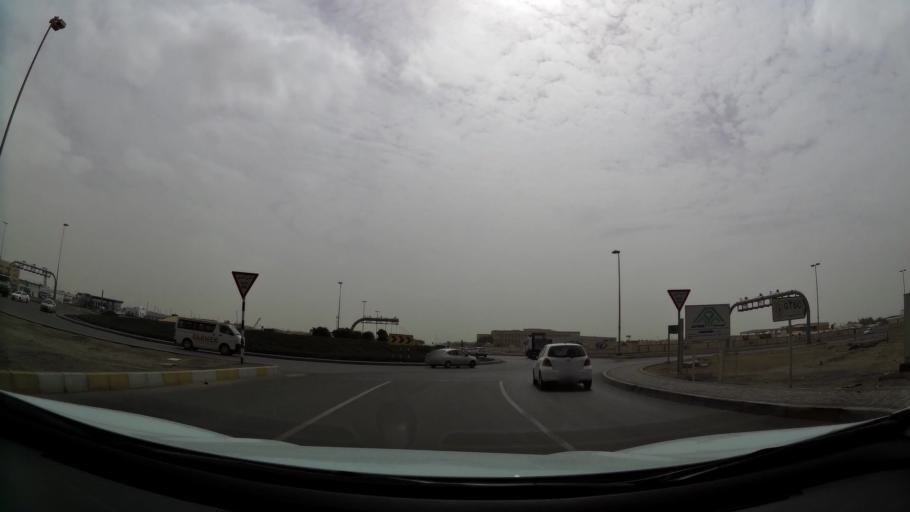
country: AE
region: Abu Dhabi
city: Abu Dhabi
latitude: 24.3587
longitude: 54.4720
